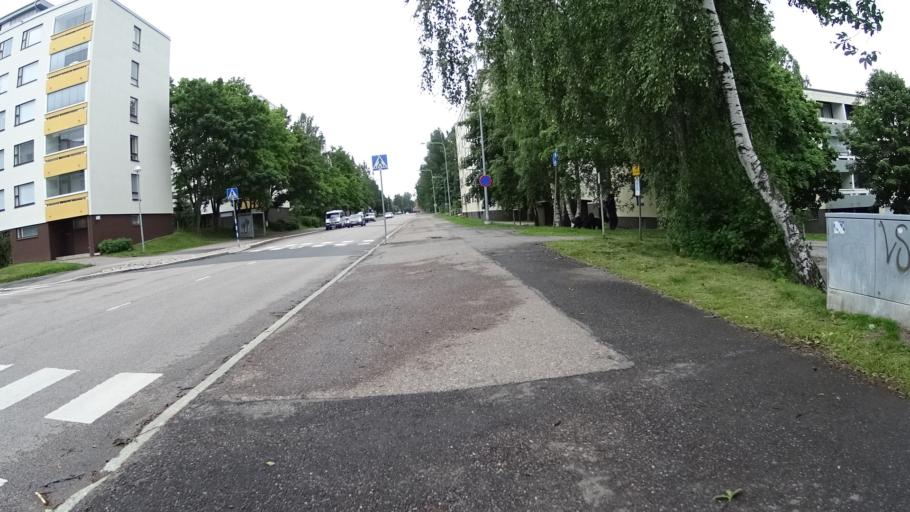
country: FI
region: Uusimaa
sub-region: Helsinki
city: Kilo
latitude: 60.2570
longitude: 24.8272
